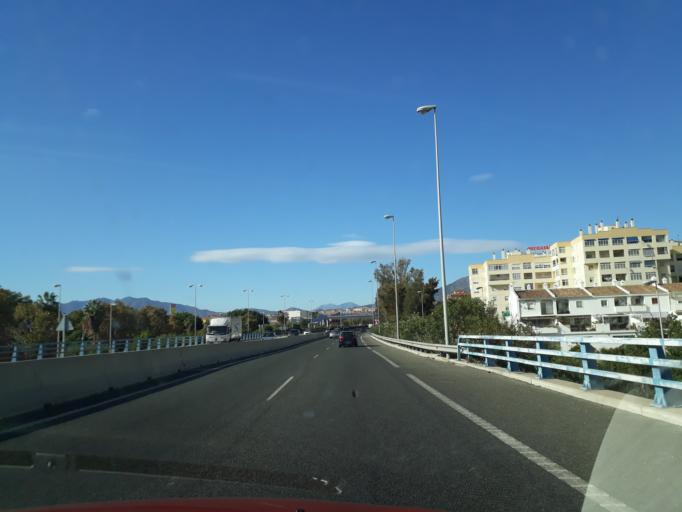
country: ES
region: Andalusia
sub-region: Provincia de Malaga
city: Fuengirola
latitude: 36.5317
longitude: -4.6300
